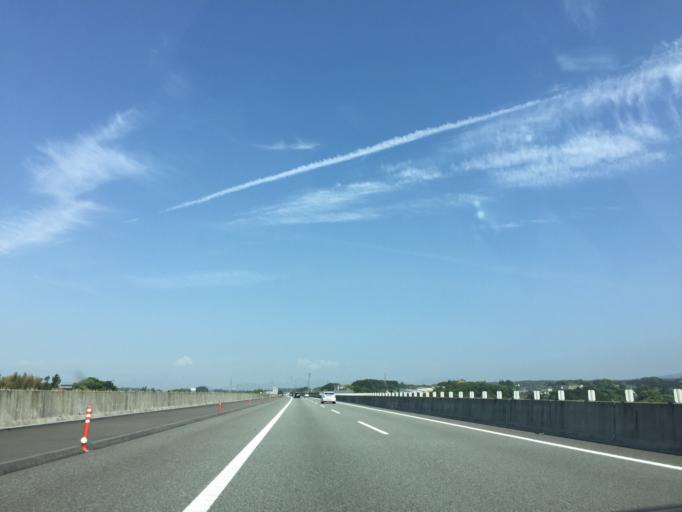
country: JP
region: Shizuoka
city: Fuji
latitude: 35.1822
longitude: 138.7284
